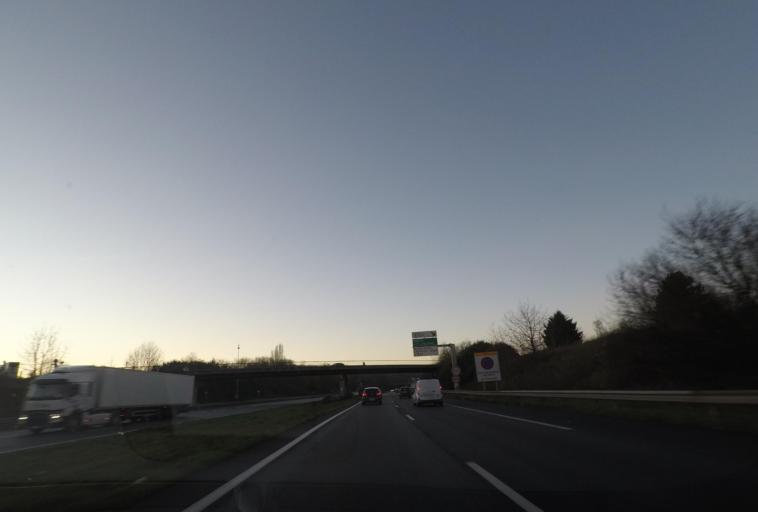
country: FR
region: Ile-de-France
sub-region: Departement de l'Essonne
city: Leuville-sur-Orge
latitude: 48.6235
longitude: 2.2679
